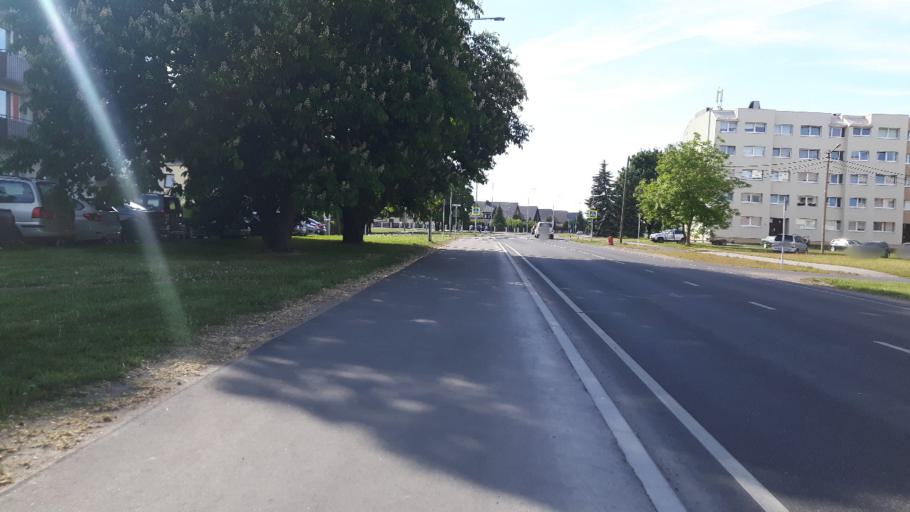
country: EE
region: Harju
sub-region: Joelaehtme vald
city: Loo
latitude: 59.4352
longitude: 24.9439
